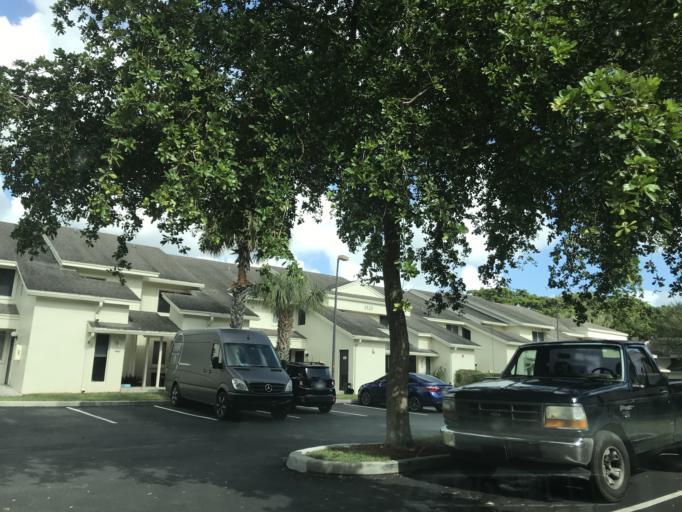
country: US
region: Florida
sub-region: Broward County
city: Coconut Creek
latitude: 26.2722
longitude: -80.1937
